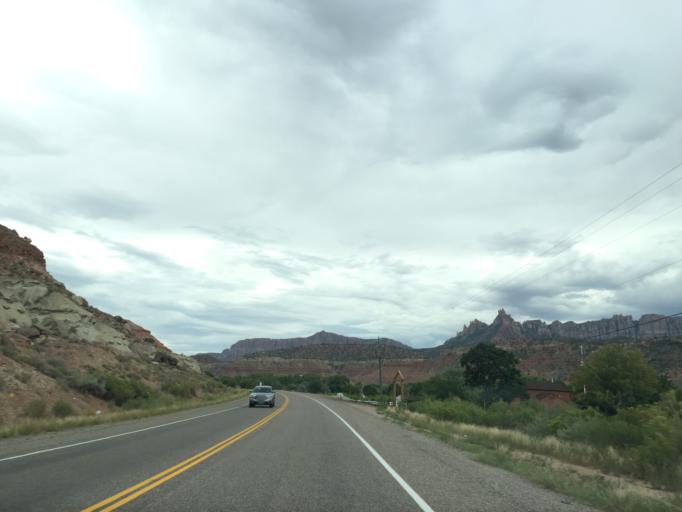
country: US
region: Utah
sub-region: Washington County
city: Hildale
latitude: 37.1622
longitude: -113.0570
